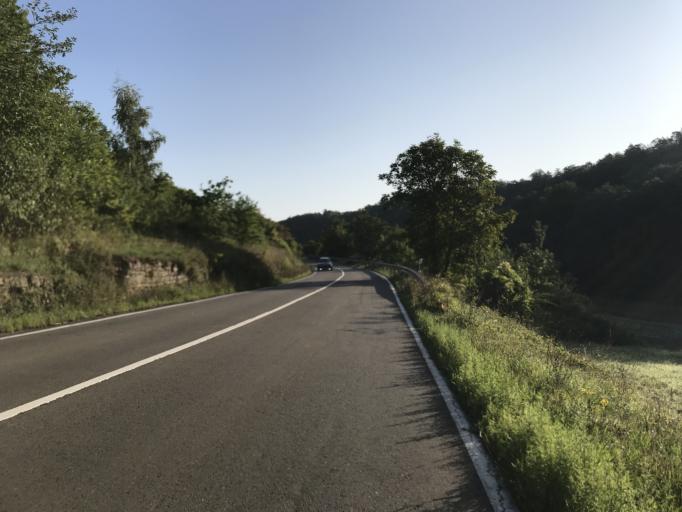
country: DE
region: Rheinland-Pfalz
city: Norheim
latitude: 49.8001
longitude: 7.8263
